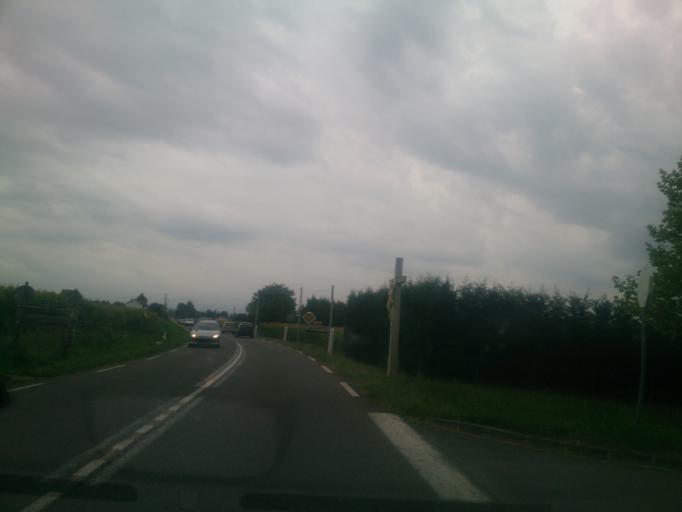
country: FR
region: Midi-Pyrenees
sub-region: Departement des Hautes-Pyrenees
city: Laloubere
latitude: 43.1999
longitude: 0.0768
